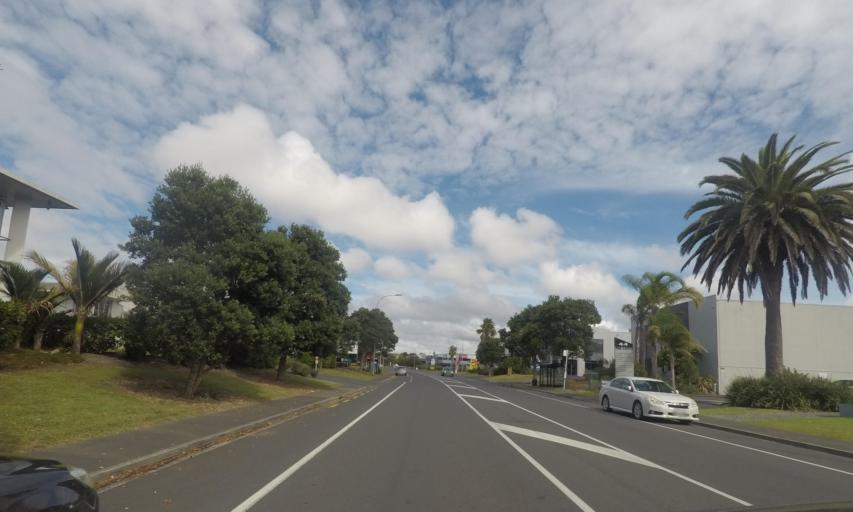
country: NZ
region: Auckland
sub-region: Auckland
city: Rothesay Bay
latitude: -36.7437
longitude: 174.6972
